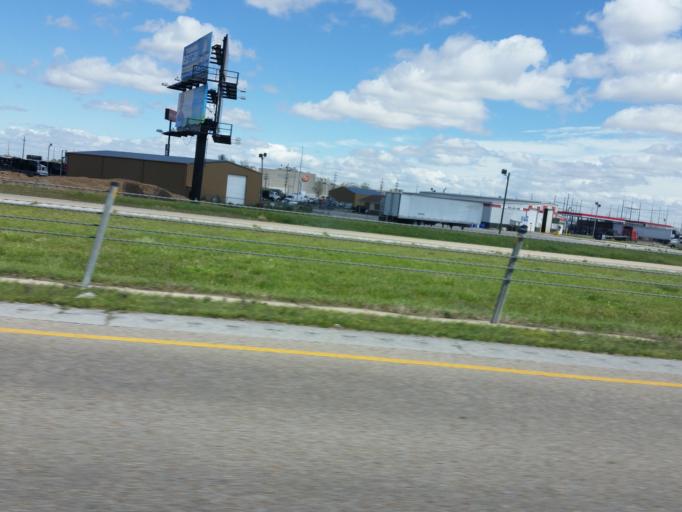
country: US
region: Arkansas
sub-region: Craighead County
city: Jonesboro
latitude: 35.8036
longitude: -90.6278
